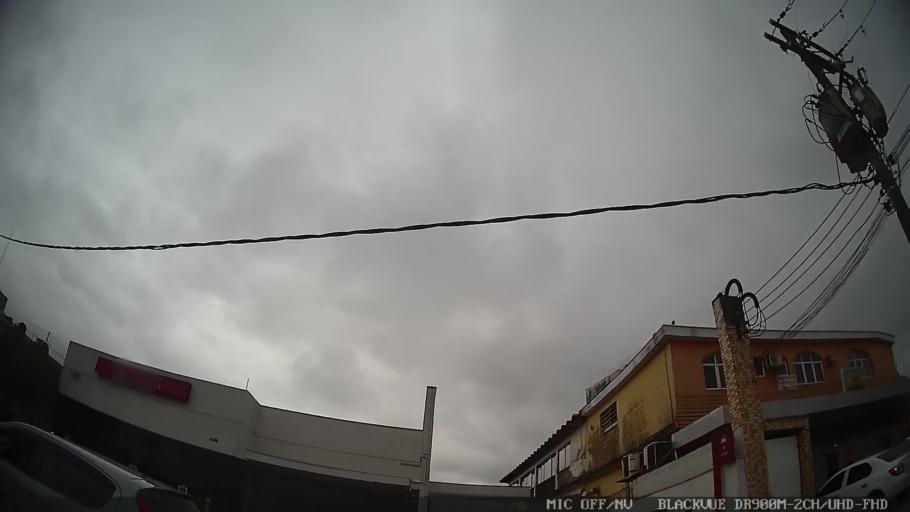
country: BR
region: Sao Paulo
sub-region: Osasco
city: Osasco
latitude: -23.4874
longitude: -46.7478
